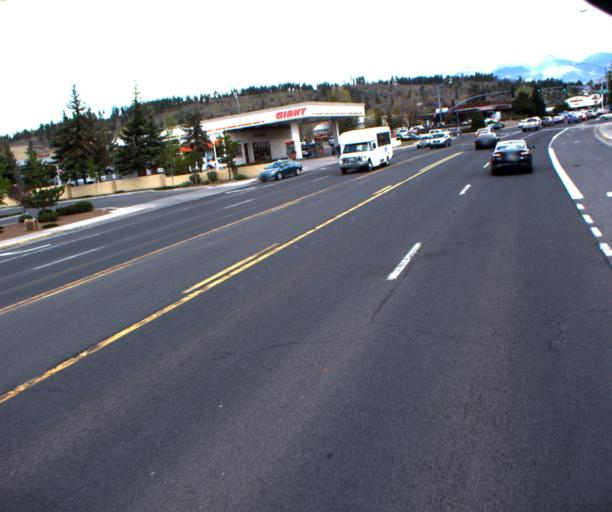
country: US
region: Arizona
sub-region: Coconino County
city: Flagstaff
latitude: 35.1882
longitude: -111.6615
